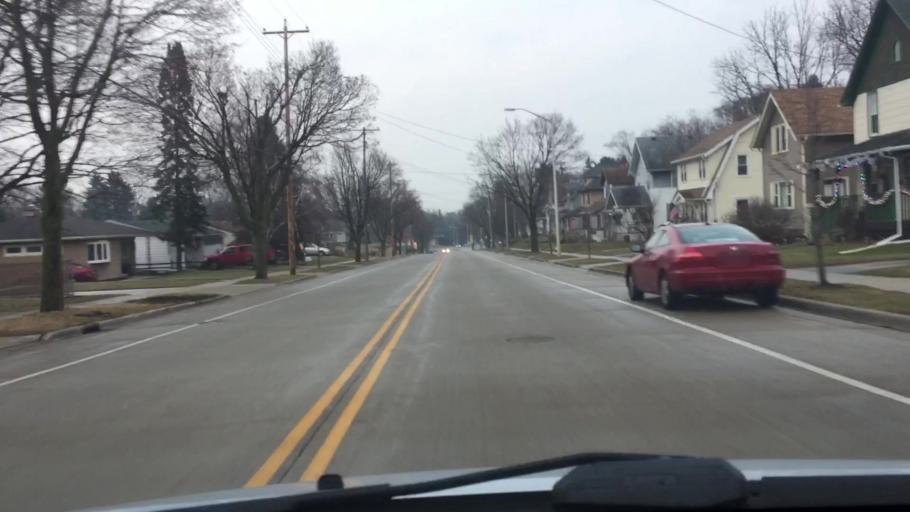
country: US
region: Wisconsin
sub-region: Waukesha County
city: Waukesha
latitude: 43.0197
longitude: -88.2438
